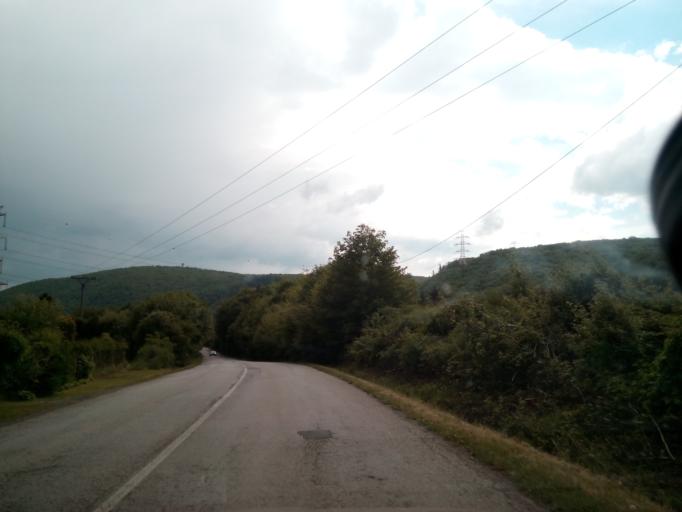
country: SK
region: Kosicky
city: Kosice
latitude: 48.7791
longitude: 21.2393
